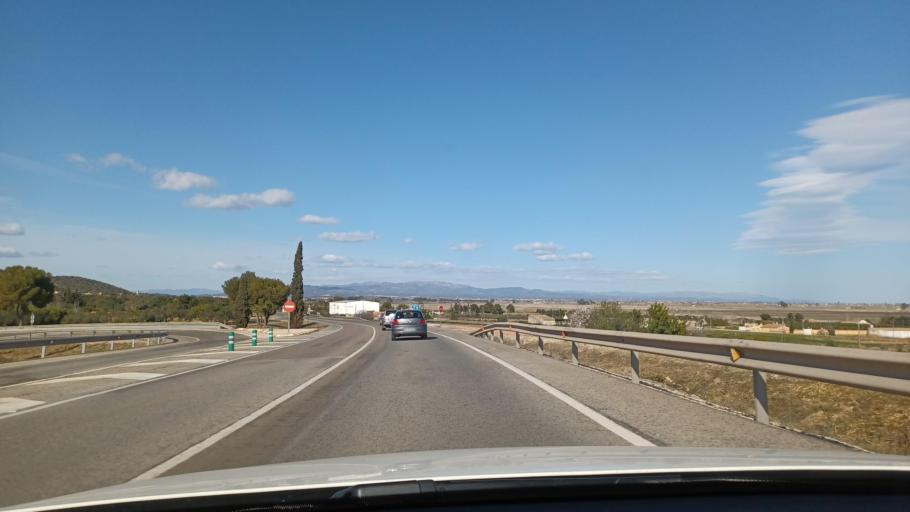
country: ES
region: Catalonia
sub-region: Provincia de Tarragona
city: Sant Carles de la Rapita
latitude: 40.6422
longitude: 0.5934
